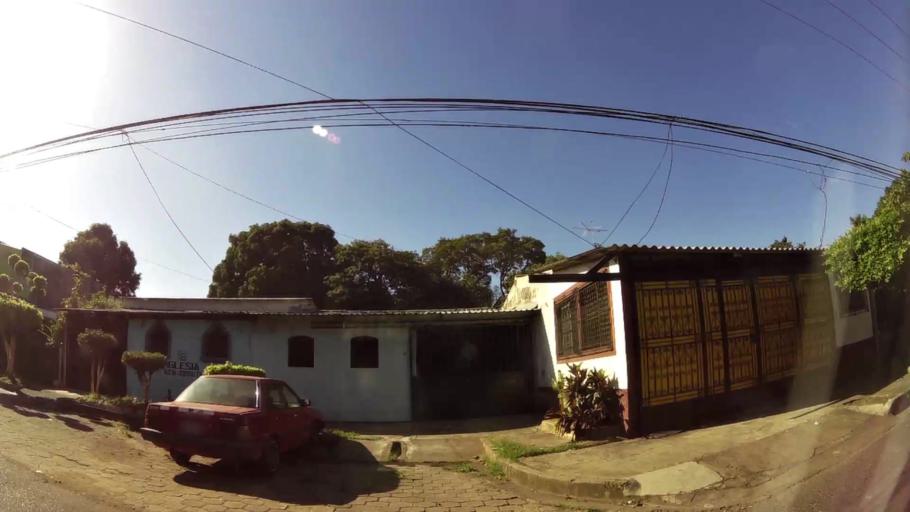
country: SV
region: Sonsonate
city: Sonzacate
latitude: 13.7321
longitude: -89.7144
